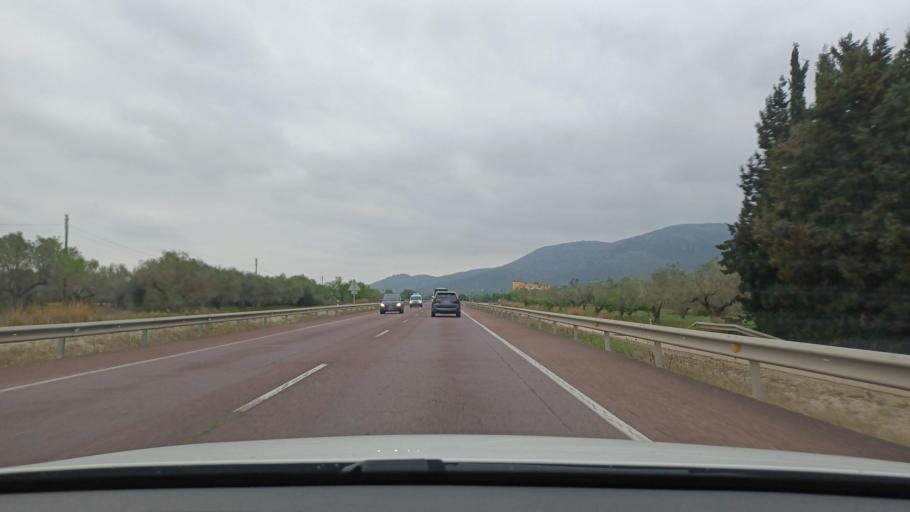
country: ES
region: Valencia
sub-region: Provincia de Castello
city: Santa Magdalena de Pulpis
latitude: 40.3616
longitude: 0.3064
